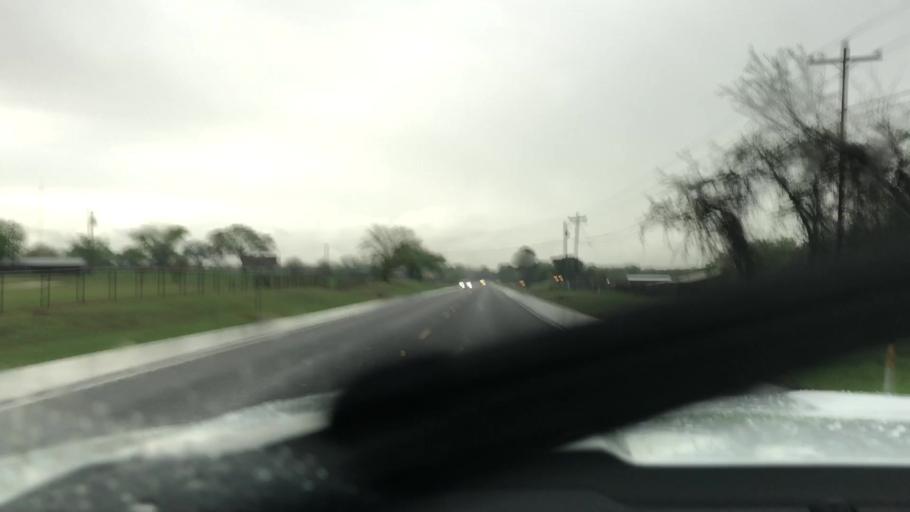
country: US
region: Texas
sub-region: Johnson County
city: Keene
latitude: 32.4393
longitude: -97.3102
